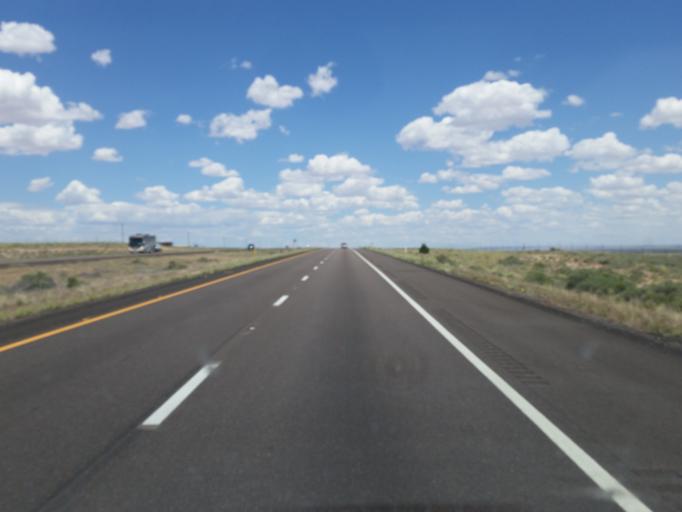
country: US
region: Arizona
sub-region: Navajo County
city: Holbrook
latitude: 34.9870
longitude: -110.0184
